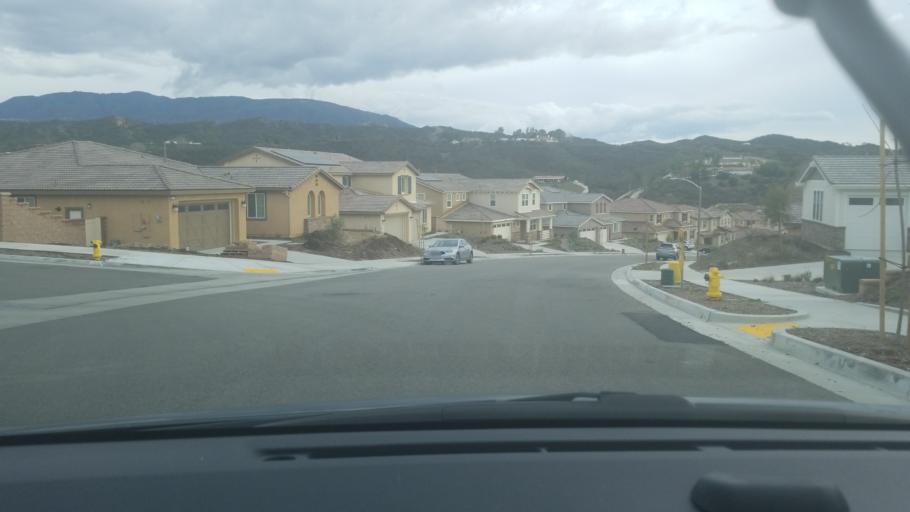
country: US
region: California
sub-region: Riverside County
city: Temecula
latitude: 33.4660
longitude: -117.0794
